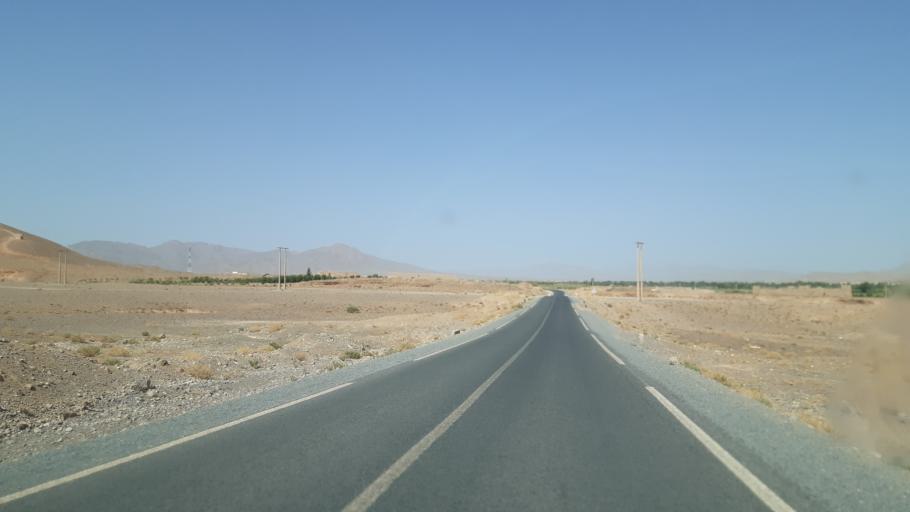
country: MA
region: Meknes-Tafilalet
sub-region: Errachidia
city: Amouguer
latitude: 32.2459
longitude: -4.5871
